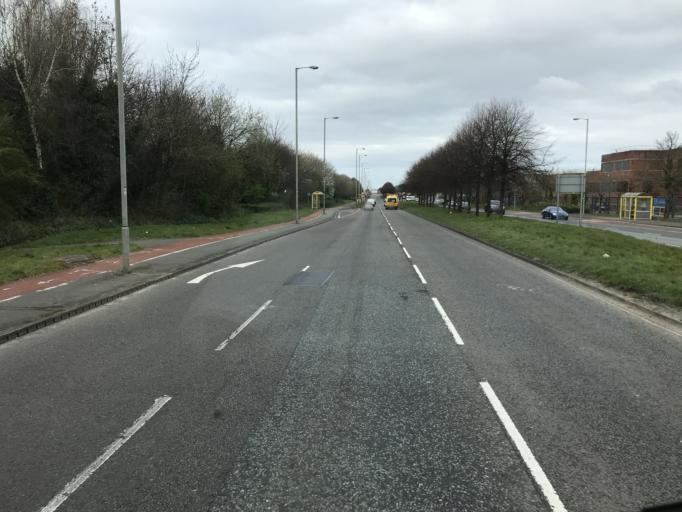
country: GB
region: England
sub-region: Borough of Halton
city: Hale
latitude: 53.3484
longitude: -2.8509
